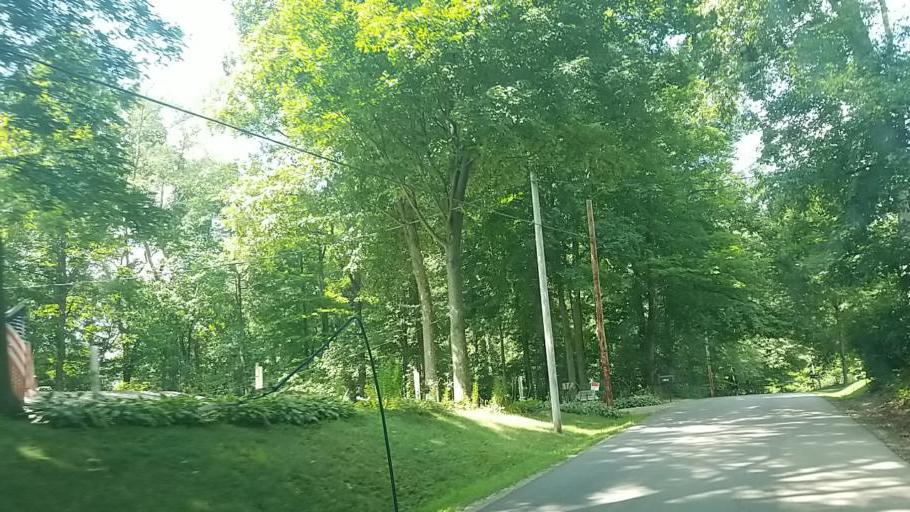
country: US
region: Ohio
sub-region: Ashland County
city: Loudonville
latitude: 40.6459
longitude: -82.3558
